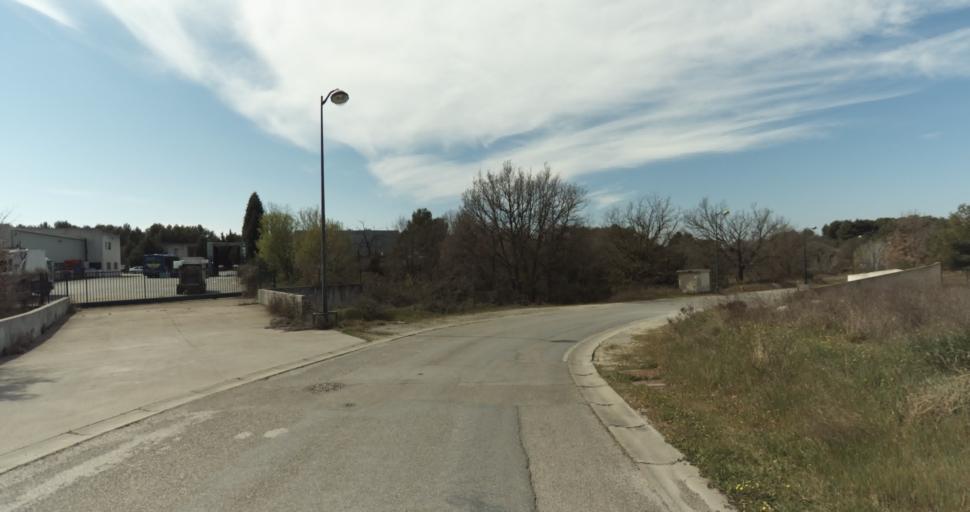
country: FR
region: Provence-Alpes-Cote d'Azur
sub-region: Departement des Bouches-du-Rhone
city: Saint-Cannat
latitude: 43.6149
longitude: 5.3153
